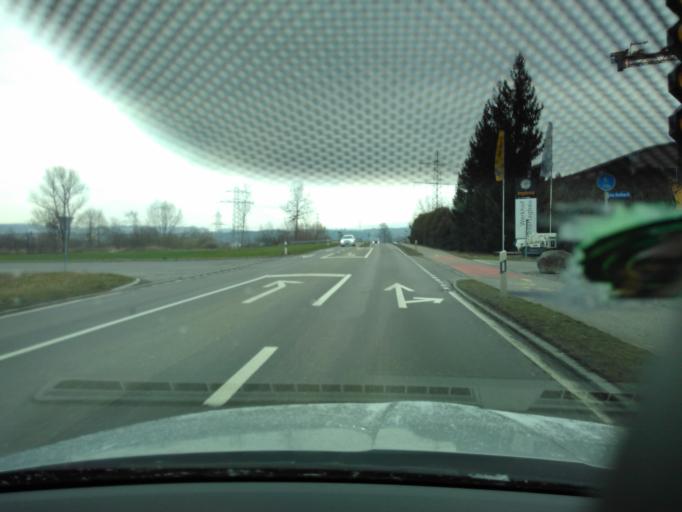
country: CH
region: Lucerne
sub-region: Lucerne-Land District
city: Buchrain
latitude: 47.1097
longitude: 8.3428
